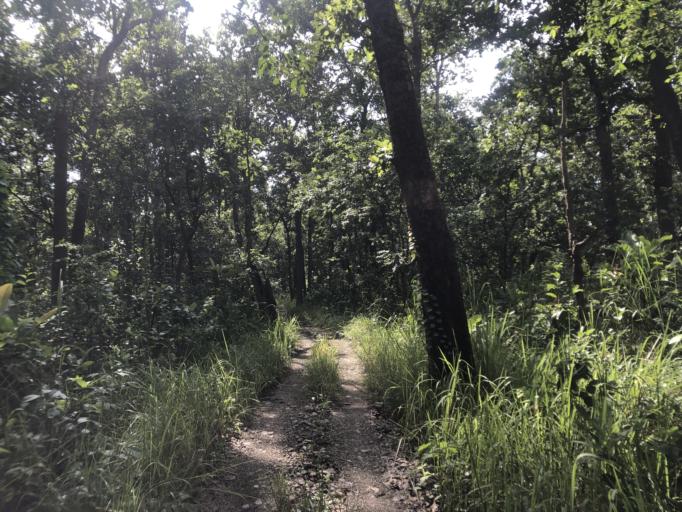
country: NP
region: Far Western
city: Tikapur
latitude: 28.5655
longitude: 81.2829
